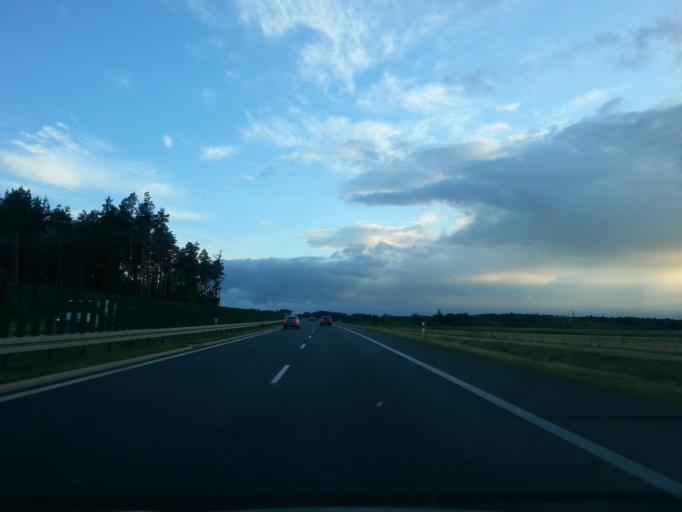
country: PL
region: Lower Silesian Voivodeship
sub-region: Powiat olesnicki
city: Miedzyborz
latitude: 51.3027
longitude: 17.5947
